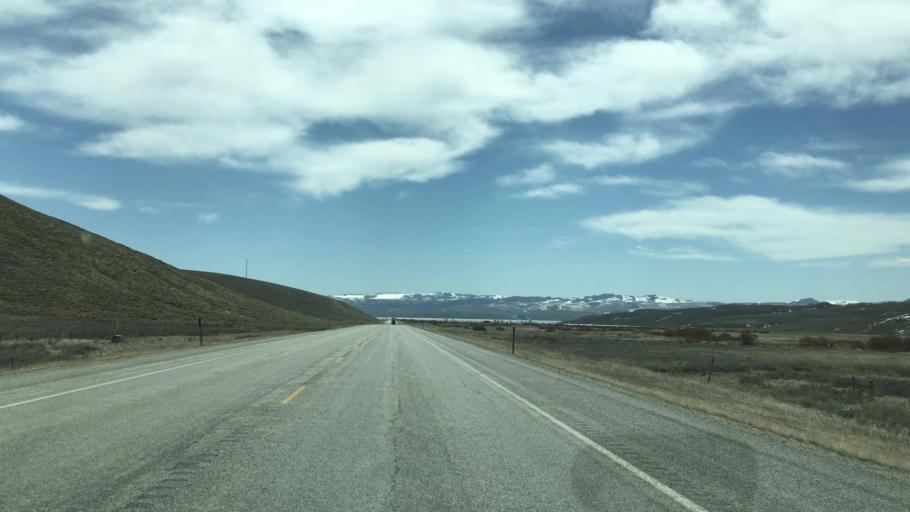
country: US
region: Utah
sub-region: Wasatch County
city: Heber
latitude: 40.2525
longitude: -111.1964
